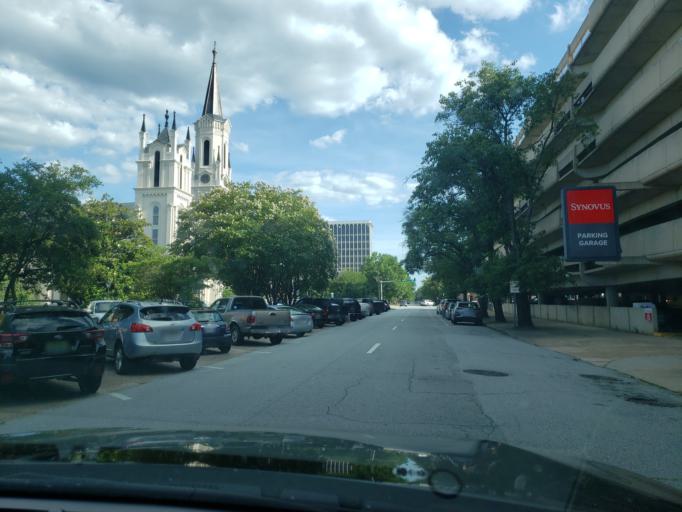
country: US
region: Georgia
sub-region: Muscogee County
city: Columbus
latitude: 32.4678
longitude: -84.9919
